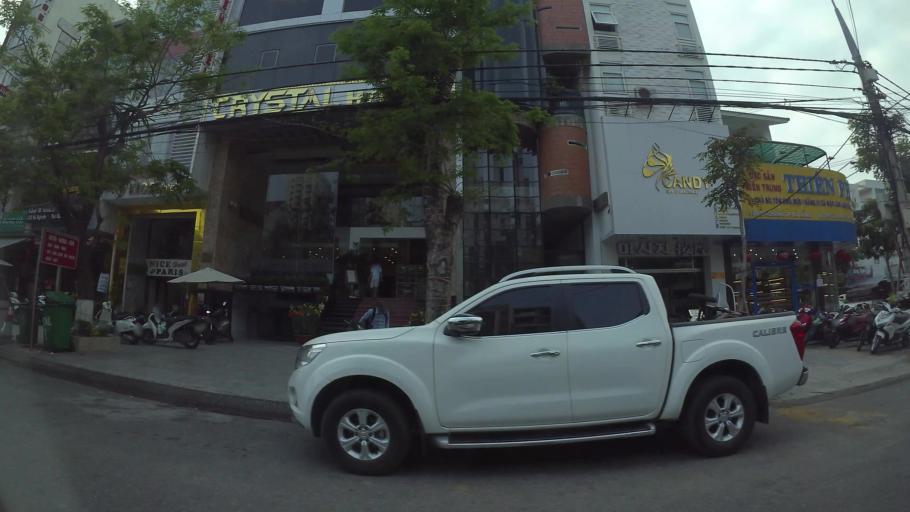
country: VN
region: Da Nang
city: Son Tra
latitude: 16.0669
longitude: 108.2432
